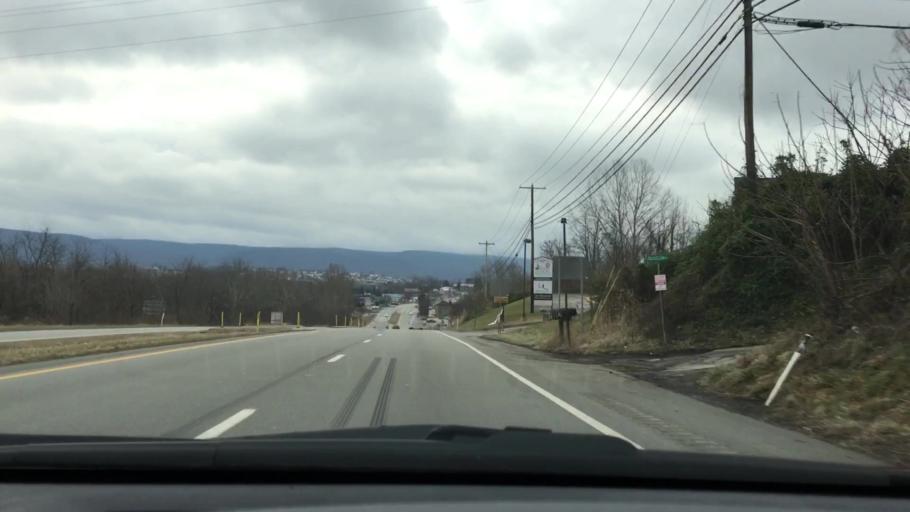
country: US
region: Pennsylvania
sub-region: Fayette County
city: Oliver
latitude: 39.9317
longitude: -79.7290
